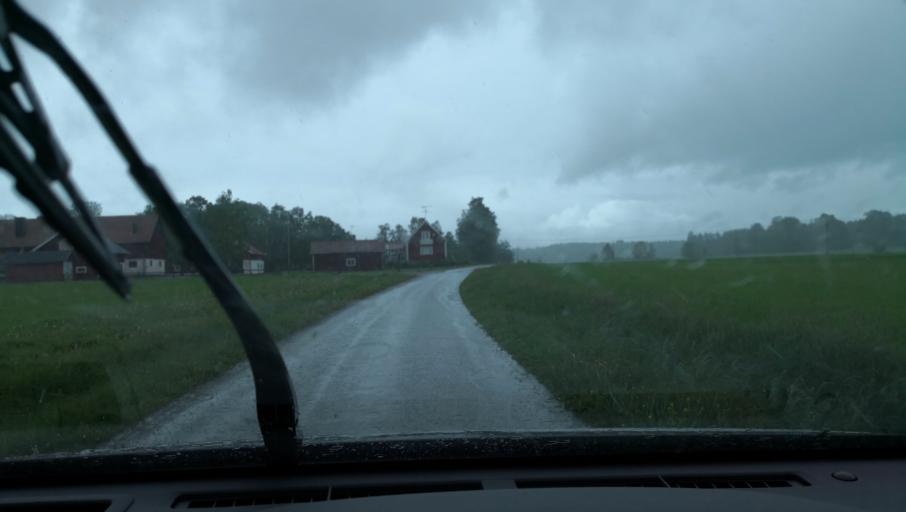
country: SE
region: Uppsala
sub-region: Enkopings Kommun
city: Orsundsbro
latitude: 59.7783
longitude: 17.3495
